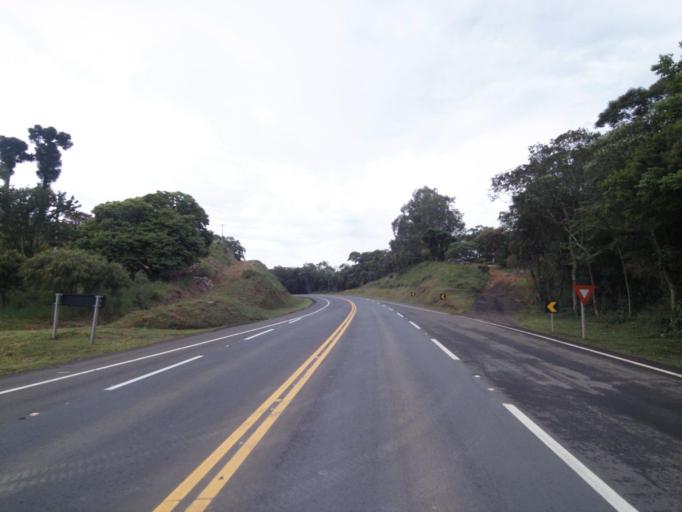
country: BR
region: Parana
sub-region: Irati
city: Irati
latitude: -25.4535
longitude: -50.6502
